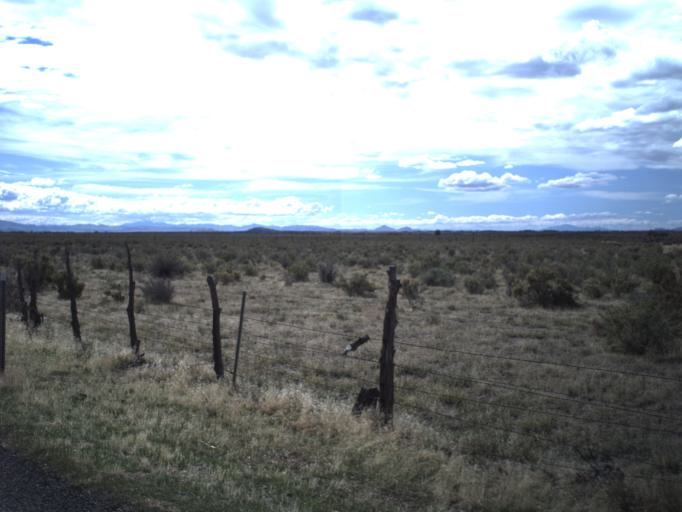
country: US
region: Utah
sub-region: Millard County
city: Fillmore
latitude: 39.0827
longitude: -112.4099
